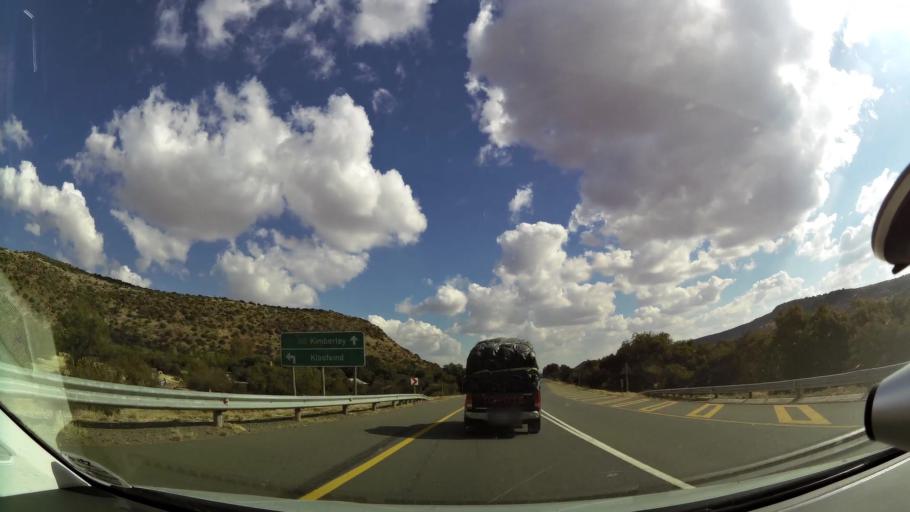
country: ZA
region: Orange Free State
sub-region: Mangaung Metropolitan Municipality
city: Bloemfontein
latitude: -29.1589
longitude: 26.0524
